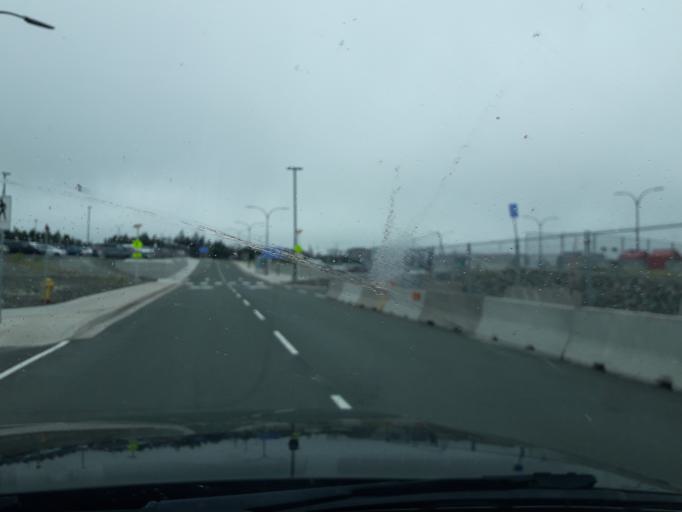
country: CA
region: Newfoundland and Labrador
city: Torbay
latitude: 47.6129
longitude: -52.7452
